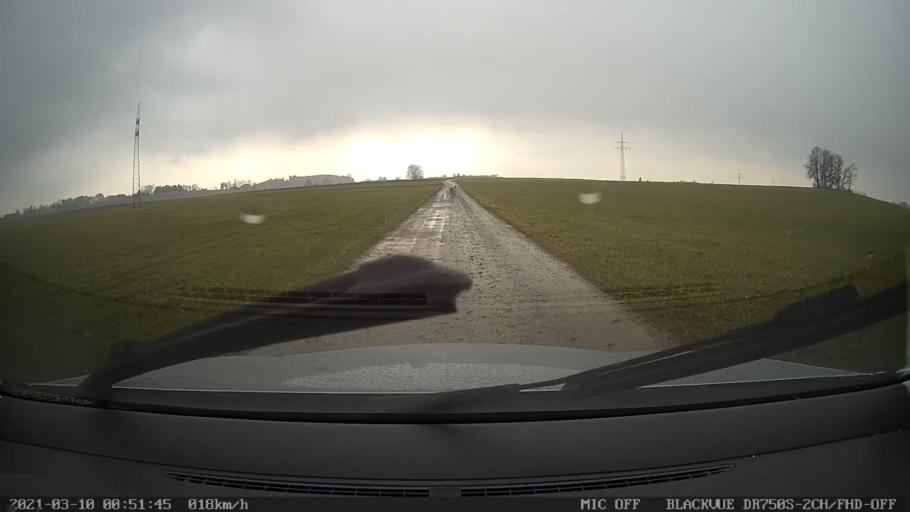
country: DE
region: Bavaria
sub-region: Upper Bavaria
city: Griesstatt
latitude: 47.9941
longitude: 12.1916
